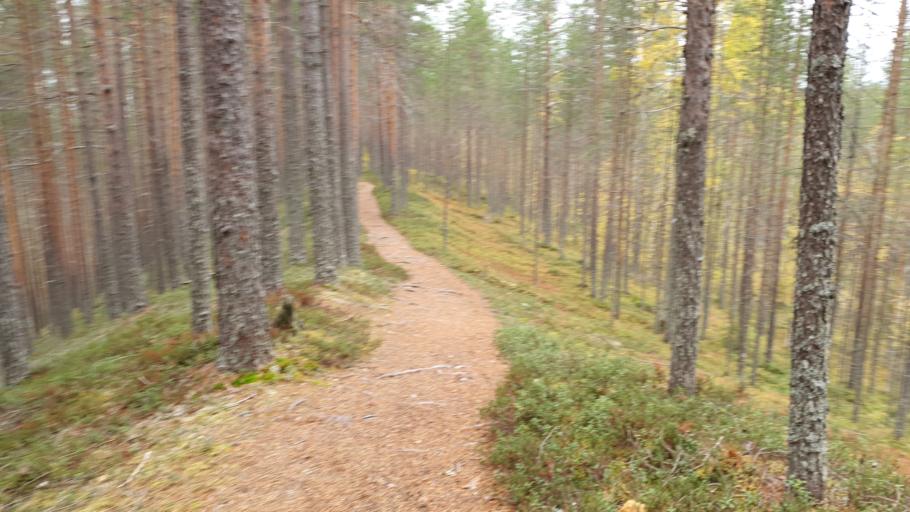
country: FI
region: Kainuu
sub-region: Kehys-Kainuu
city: Kuhmo
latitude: 64.2927
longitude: 29.3637
